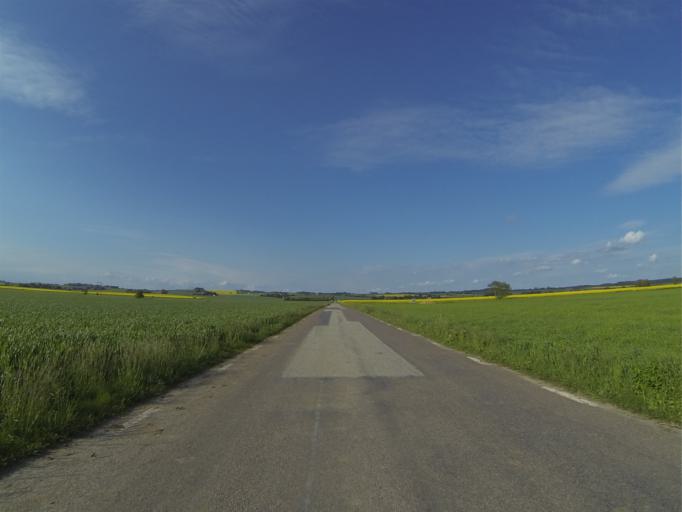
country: SE
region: Skane
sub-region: Staffanstorps Kommun
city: Staffanstorp
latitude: 55.6671
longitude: 13.2723
